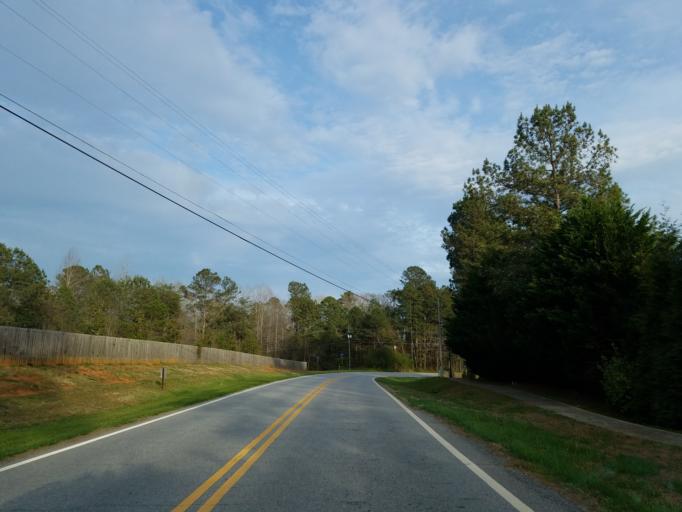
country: US
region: Georgia
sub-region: Dawson County
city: Dawsonville
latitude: 34.4279
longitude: -84.1223
